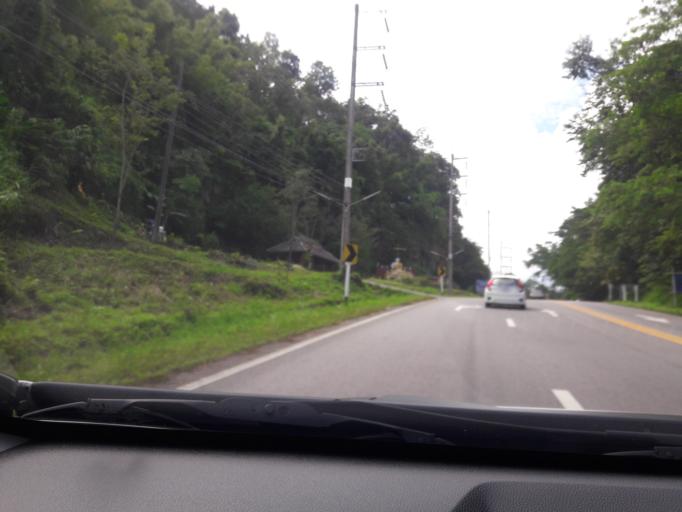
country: TH
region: Chiang Mai
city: Mae Taeng
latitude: 19.1249
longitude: 98.7638
